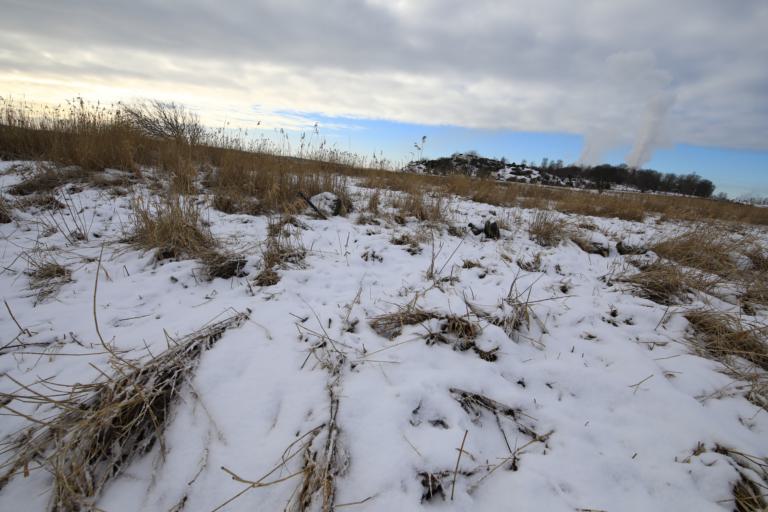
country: SE
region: Halland
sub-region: Kungsbacka Kommun
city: Frillesas
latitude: 57.2271
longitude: 12.2056
